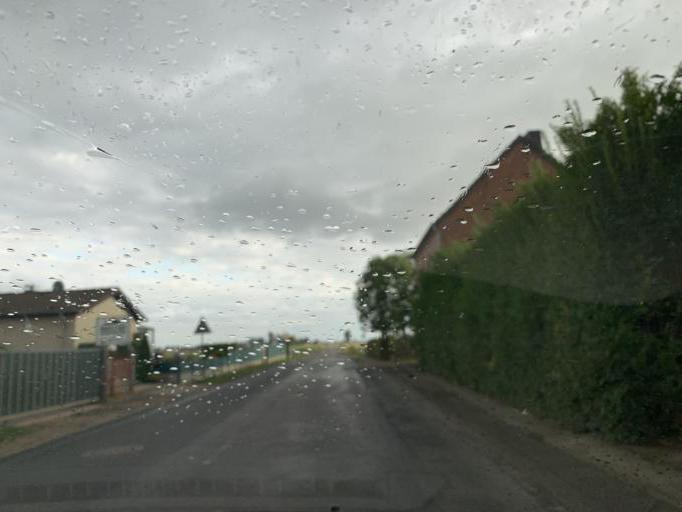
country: DE
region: North Rhine-Westphalia
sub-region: Regierungsbezirk Koln
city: Linnich
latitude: 50.9628
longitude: 6.2762
